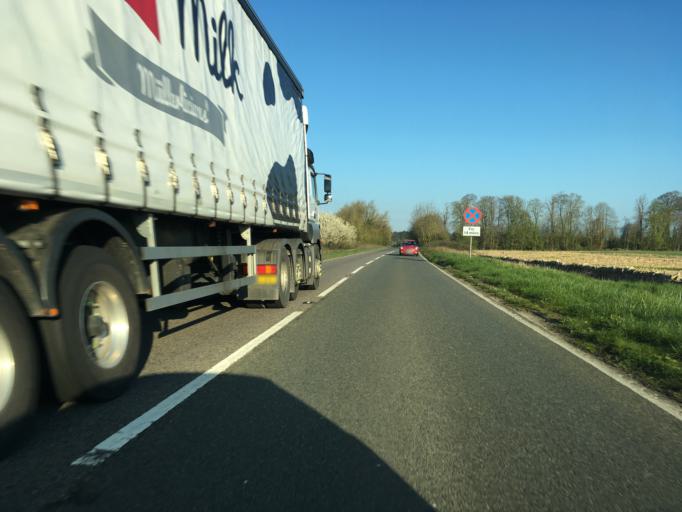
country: GB
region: England
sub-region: Oxfordshire
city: Burford
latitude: 51.8086
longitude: -1.6653
